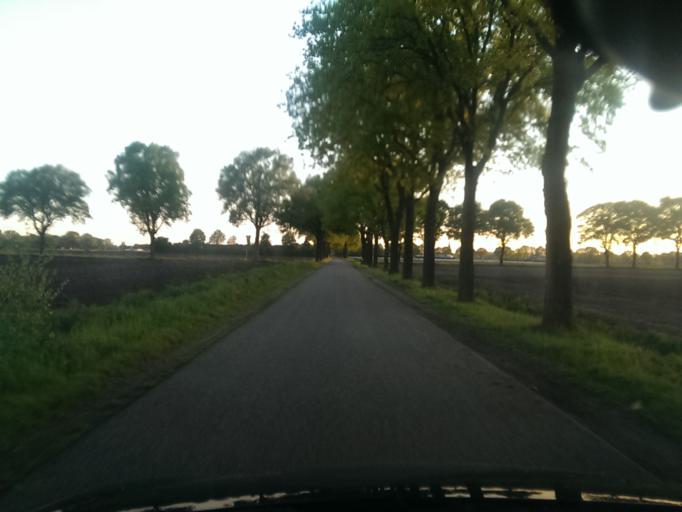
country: NL
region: Limburg
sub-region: Gemeente Nederweert
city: Nederweert
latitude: 51.3019
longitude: 5.8064
